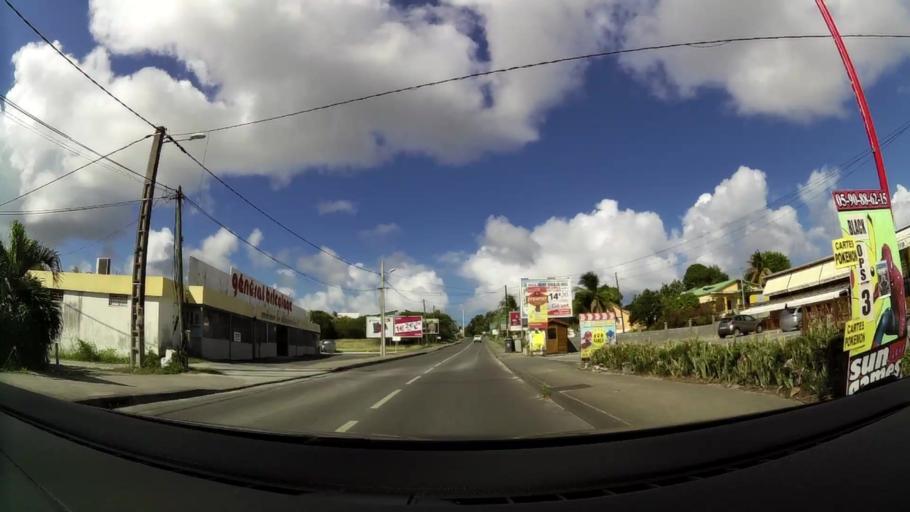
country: GP
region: Guadeloupe
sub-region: Guadeloupe
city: Saint-Francois
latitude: 16.2541
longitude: -61.2895
